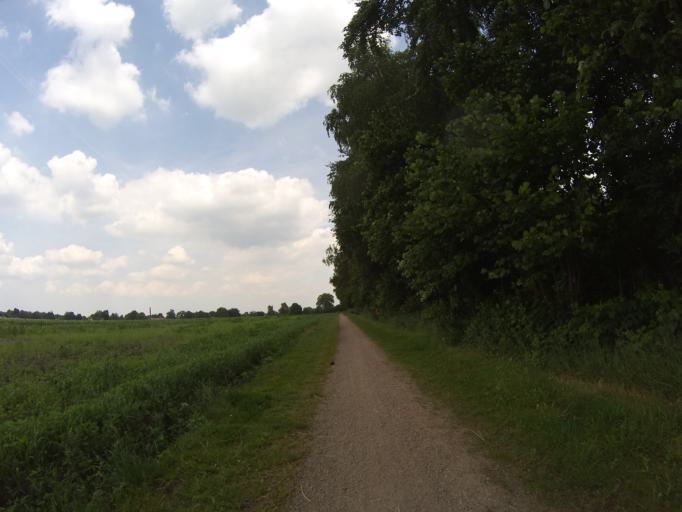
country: NL
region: Utrecht
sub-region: Gemeente Soest
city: Soest
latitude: 52.1727
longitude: 5.3070
